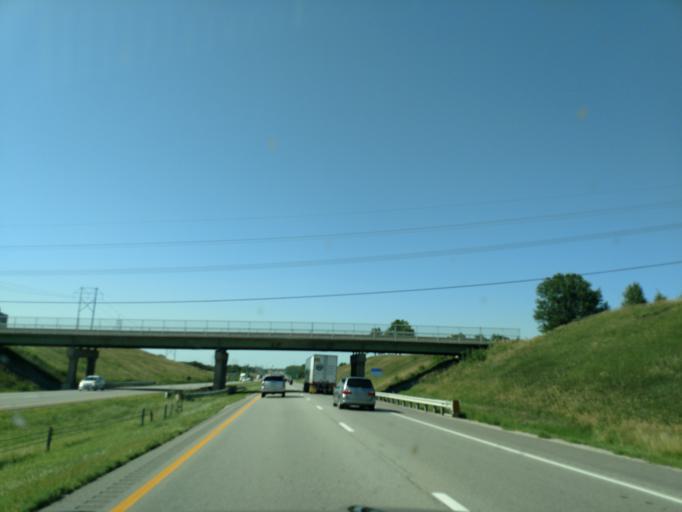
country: US
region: Missouri
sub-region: Buchanan County
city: Saint Joseph
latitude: 39.7542
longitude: -94.7900
